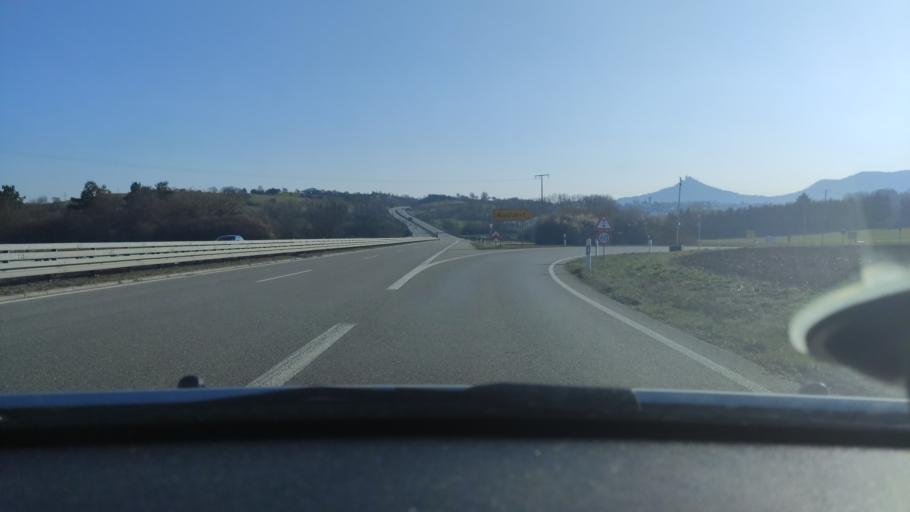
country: DE
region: Baden-Wuerttemberg
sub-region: Tuebingen Region
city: Grosselfingen
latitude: 48.3110
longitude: 8.8845
